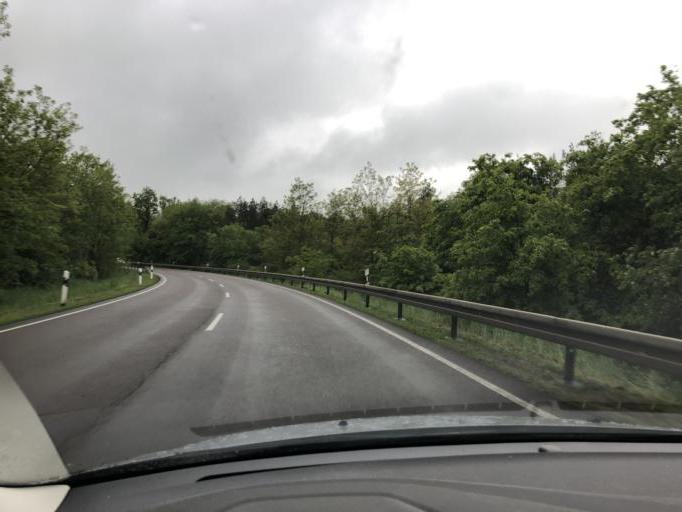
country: DE
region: Saxony-Anhalt
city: Dessau
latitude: 51.7927
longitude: 12.2337
